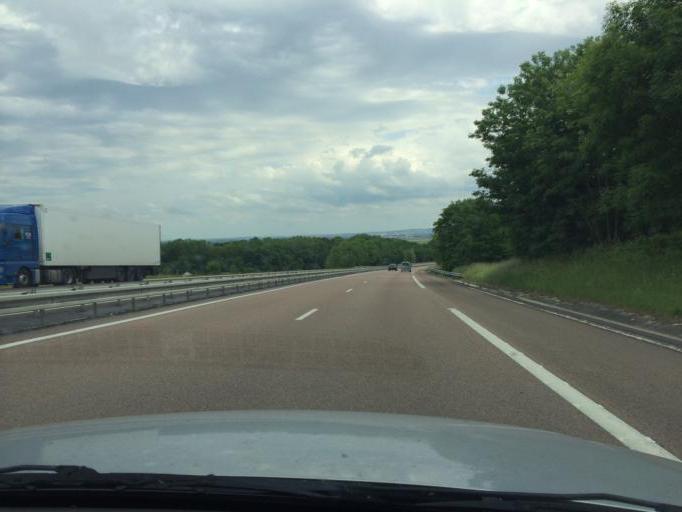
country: FR
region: Champagne-Ardenne
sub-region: Departement de la Marne
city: Gueux
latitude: 49.2423
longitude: 3.8879
